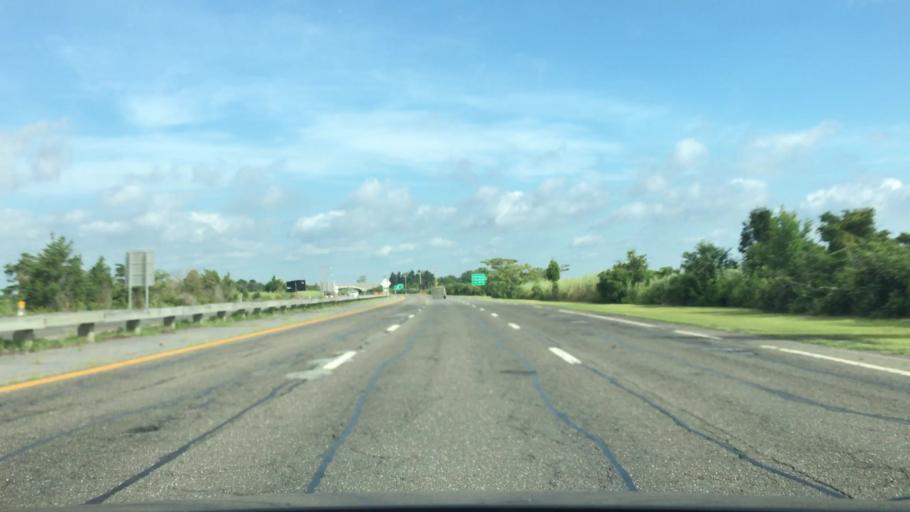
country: US
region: New York
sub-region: Nassau County
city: Point Lookout
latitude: 40.6057
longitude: -73.5453
